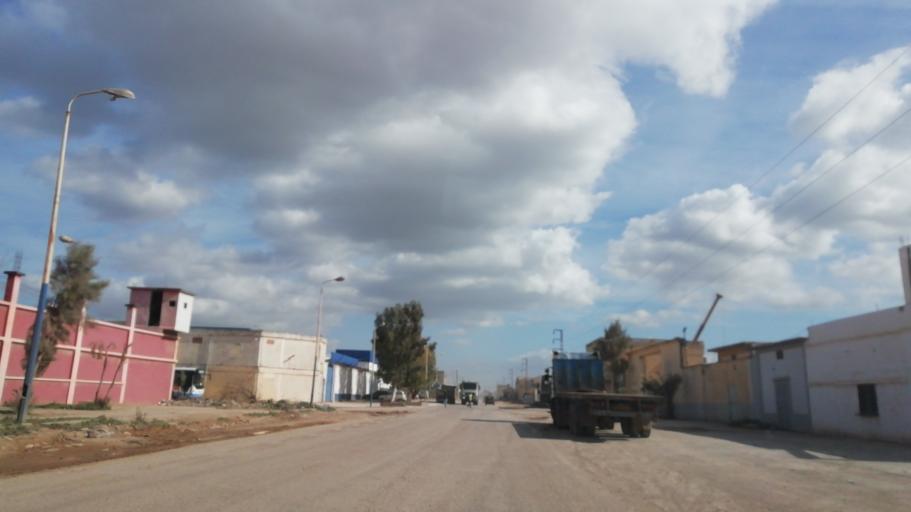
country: DZ
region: Oran
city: Es Senia
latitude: 35.6512
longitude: -0.5859
